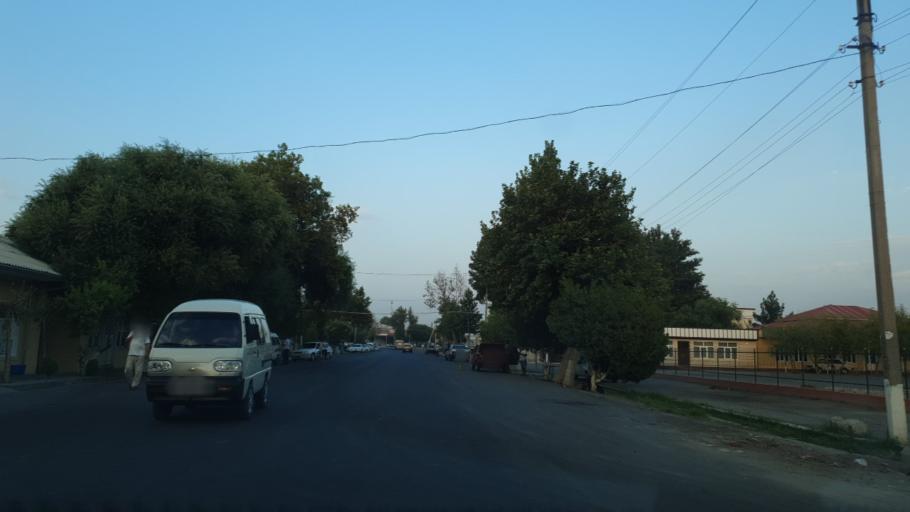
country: UZ
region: Fergana
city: Beshariq
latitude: 40.4361
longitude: 70.6001
